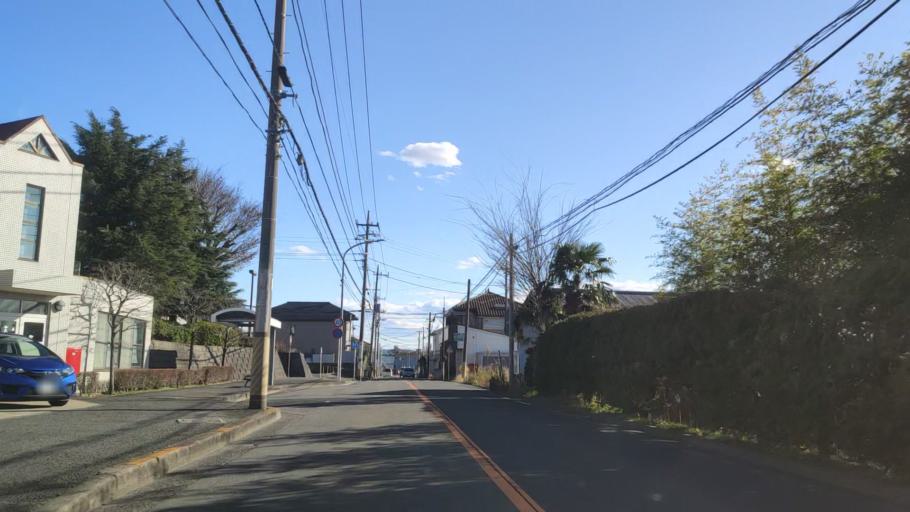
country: JP
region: Tokyo
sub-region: Machida-shi
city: Machida
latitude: 35.5237
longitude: 139.5339
